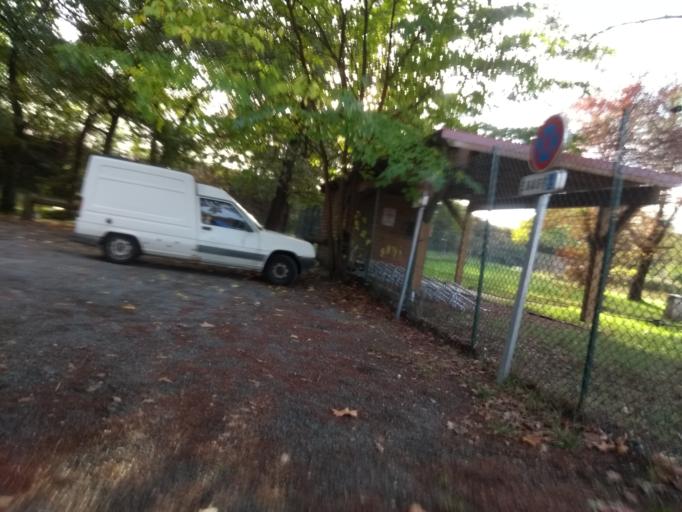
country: FR
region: Aquitaine
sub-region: Departement de la Gironde
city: Pessac
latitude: 44.7887
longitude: -0.6402
